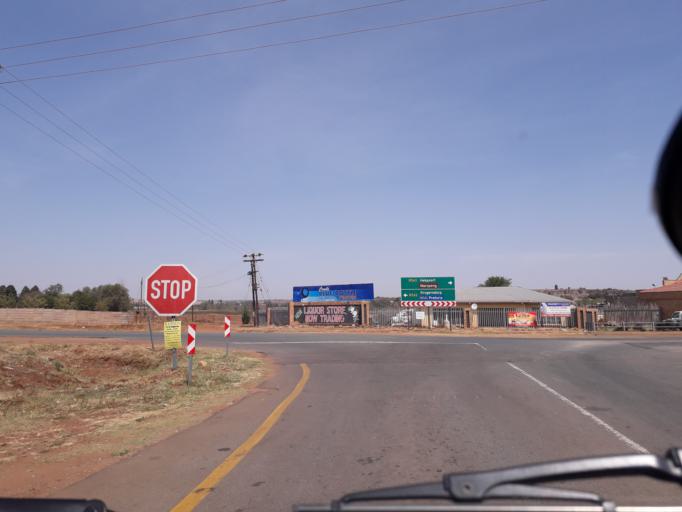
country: ZA
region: Gauteng
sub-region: West Rand District Municipality
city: Krugersdorp
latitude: -26.0227
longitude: 27.7237
